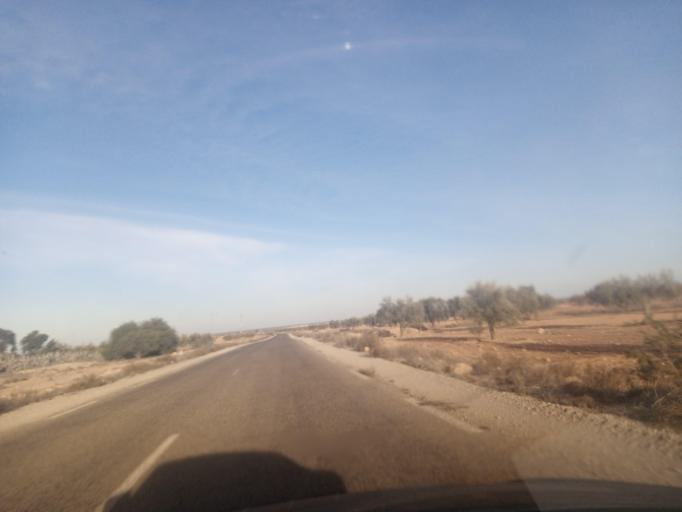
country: TN
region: Safaqis
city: Bi'r `Ali Bin Khalifah
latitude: 34.9375
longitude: 10.3378
